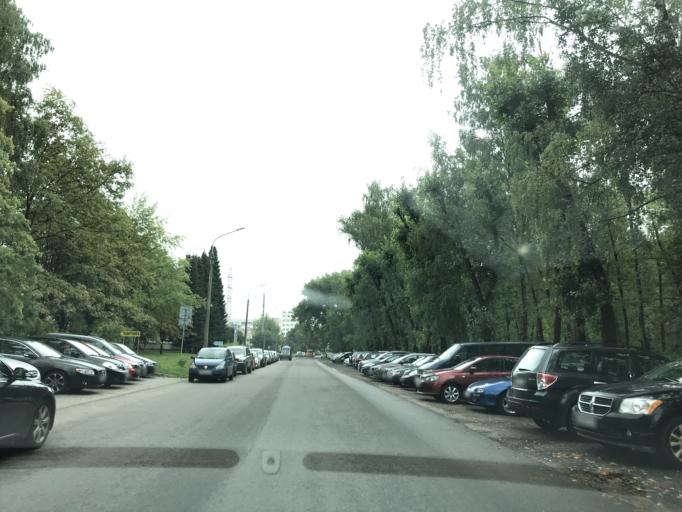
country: BY
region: Minsk
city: Minsk
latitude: 53.9462
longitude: 27.6161
